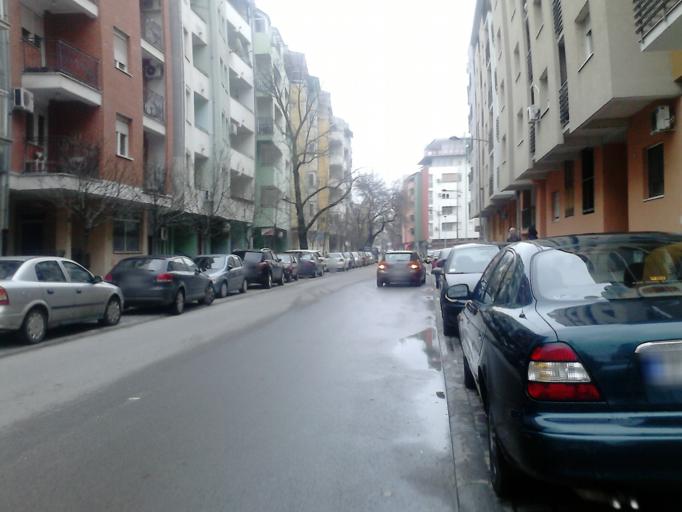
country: RS
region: Autonomna Pokrajina Vojvodina
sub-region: Juznobacki Okrug
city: Novi Sad
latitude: 45.2466
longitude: 19.8335
